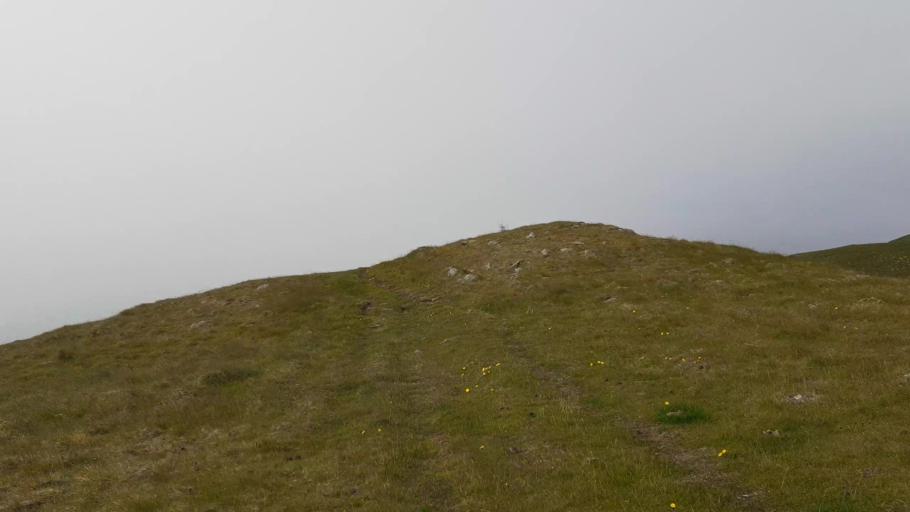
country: IS
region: Northeast
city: Dalvik
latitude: 66.5432
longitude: -17.9923
